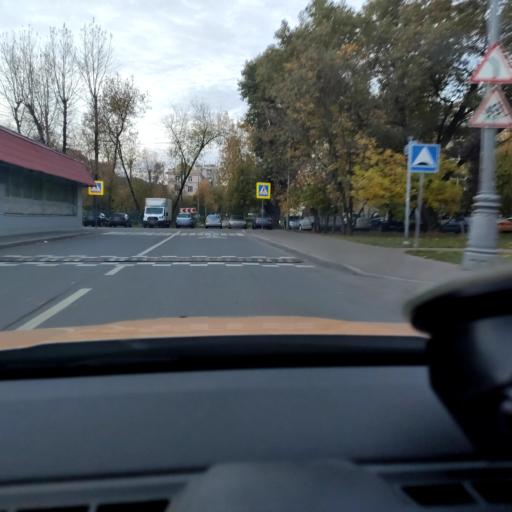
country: RU
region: Moscow
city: Yaroslavskiy
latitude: 55.8751
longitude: 37.7204
